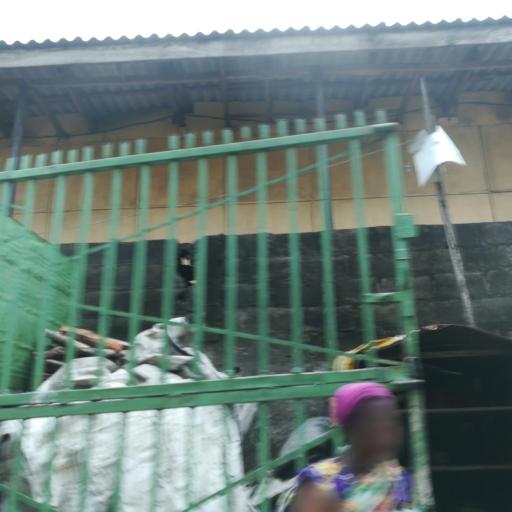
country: NG
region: Lagos
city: Makoko
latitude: 6.4990
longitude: 3.3798
